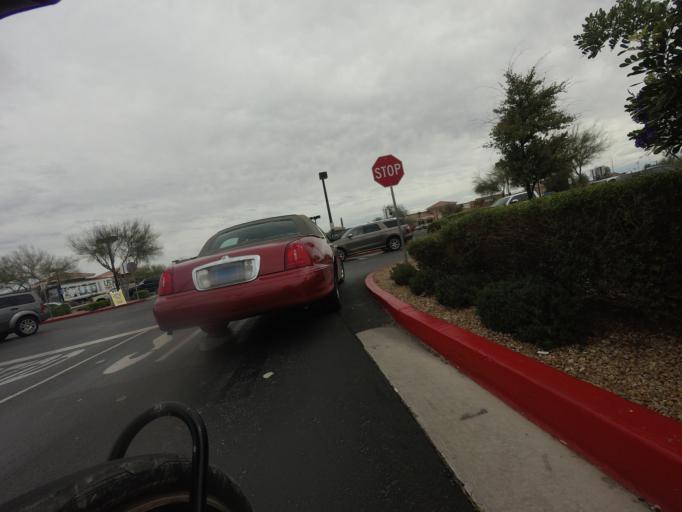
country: US
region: Nevada
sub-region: Clark County
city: North Las Vegas
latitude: 36.2790
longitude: -115.2058
